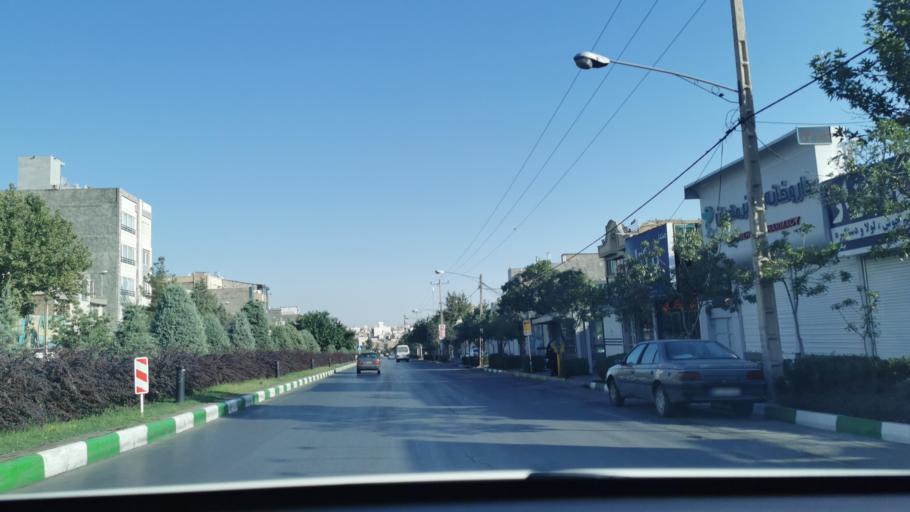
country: IR
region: Razavi Khorasan
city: Mashhad
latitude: 36.3075
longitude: 59.5081
